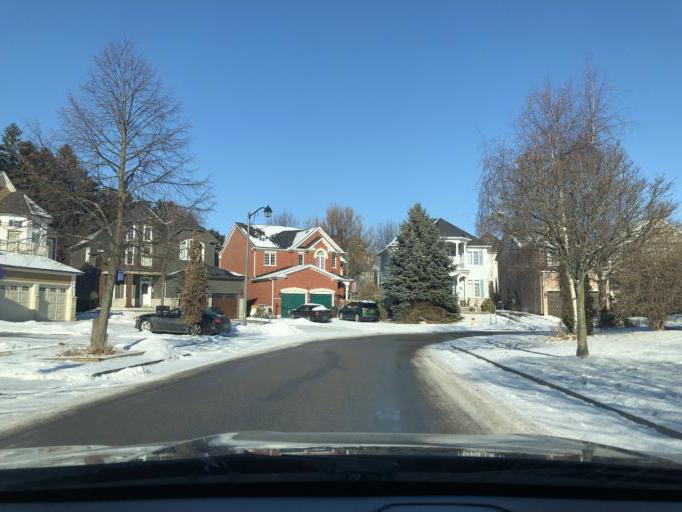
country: CA
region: Ontario
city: Scarborough
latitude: 43.7731
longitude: -79.1414
